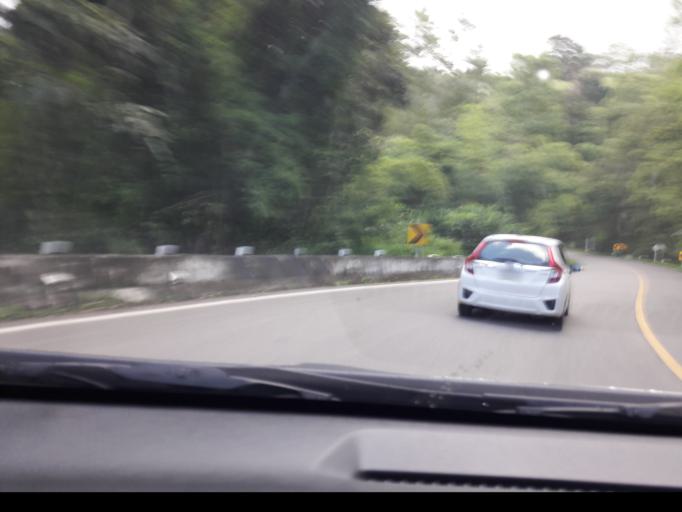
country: TH
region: Mae Hong Son
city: Sop Pong
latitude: 19.4447
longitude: 98.3437
